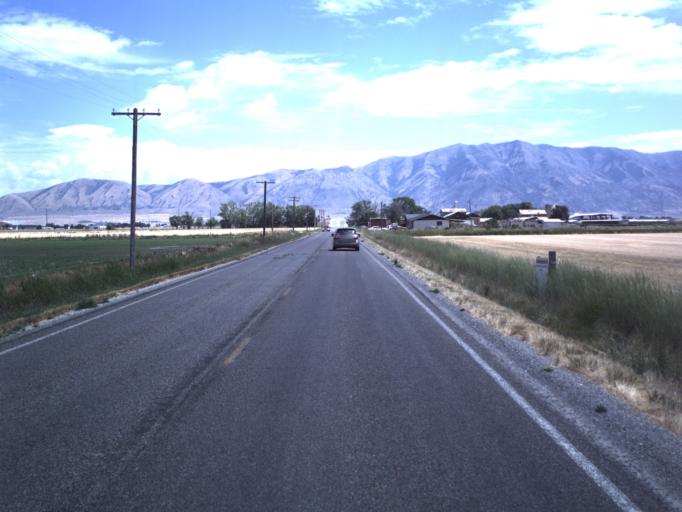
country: US
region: Utah
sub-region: Box Elder County
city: Tremonton
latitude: 41.7106
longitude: -112.2173
